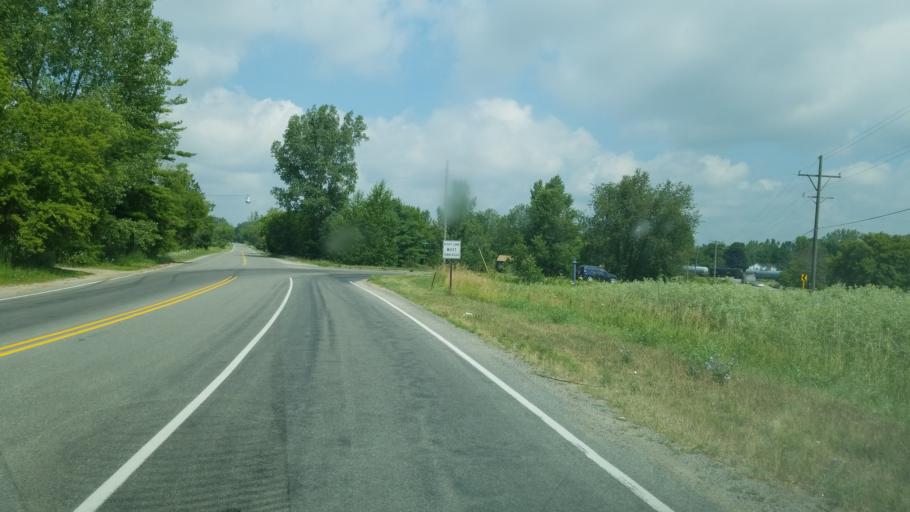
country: US
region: Michigan
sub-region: Kent County
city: Sparta
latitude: 43.1937
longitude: -85.7112
